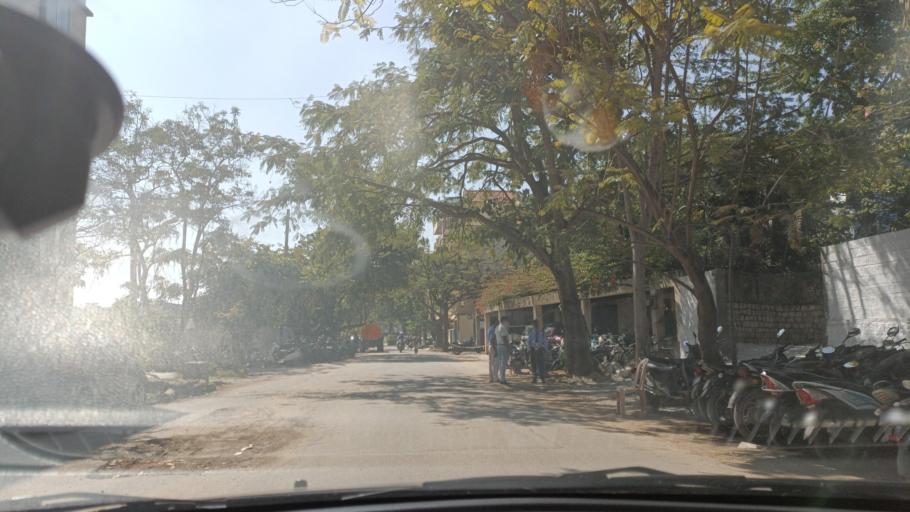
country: IN
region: Karnataka
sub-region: Bangalore Urban
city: Bangalore
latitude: 13.0330
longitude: 77.6241
